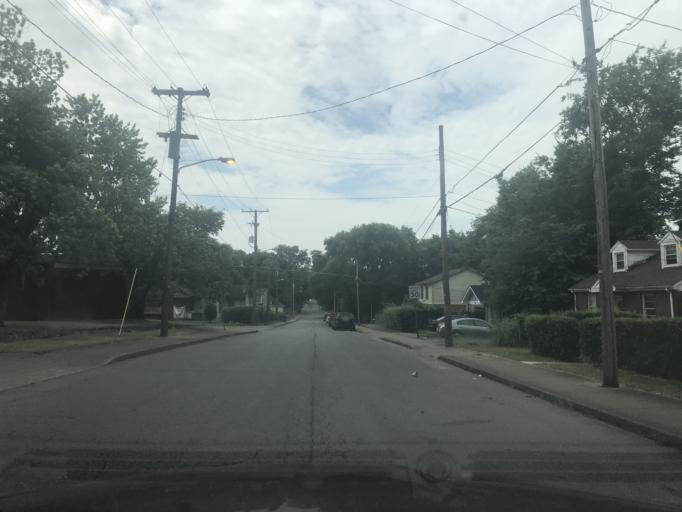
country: US
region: Tennessee
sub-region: Davidson County
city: Nashville
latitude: 36.1746
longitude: -86.8108
